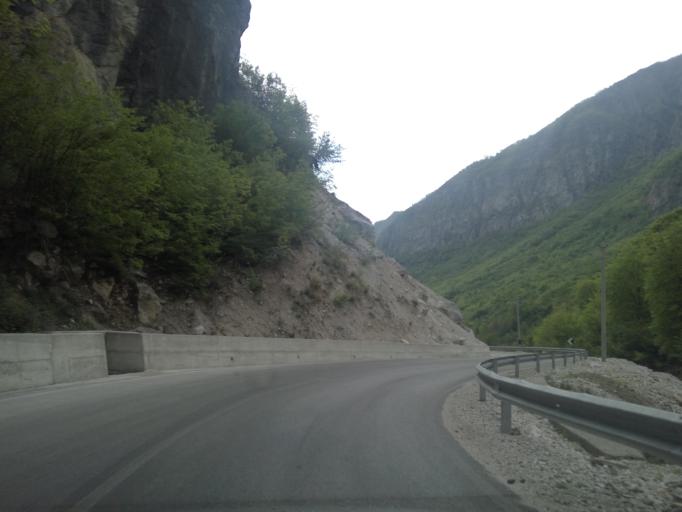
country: AL
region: Kukes
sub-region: Rrethi i Tropojes
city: Bajram Curri
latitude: 42.4027
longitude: 20.0395
